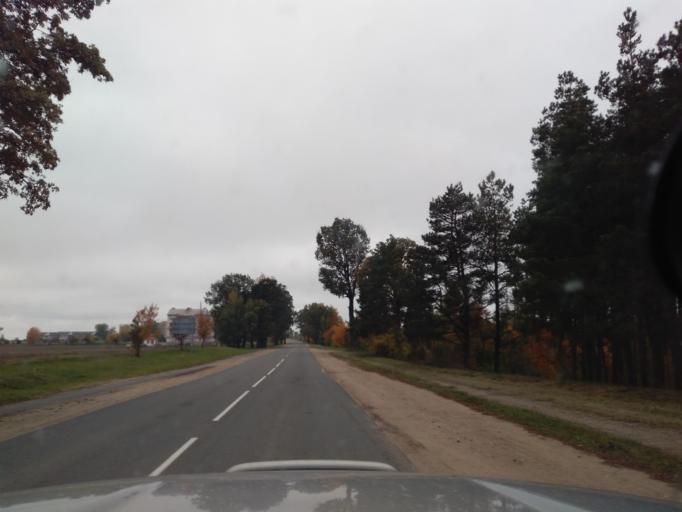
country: BY
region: Minsk
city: Kapyl'
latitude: 53.1495
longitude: 27.1222
